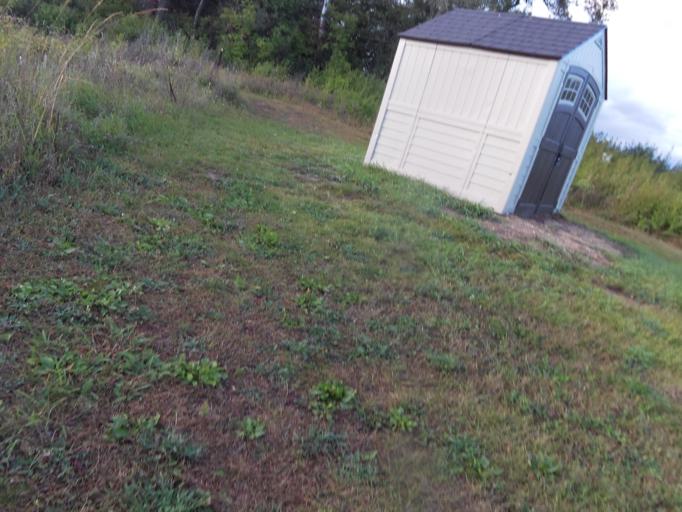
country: US
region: Minnesota
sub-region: Washington County
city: Lake Saint Croix Beach
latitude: 44.9380
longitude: -92.7847
